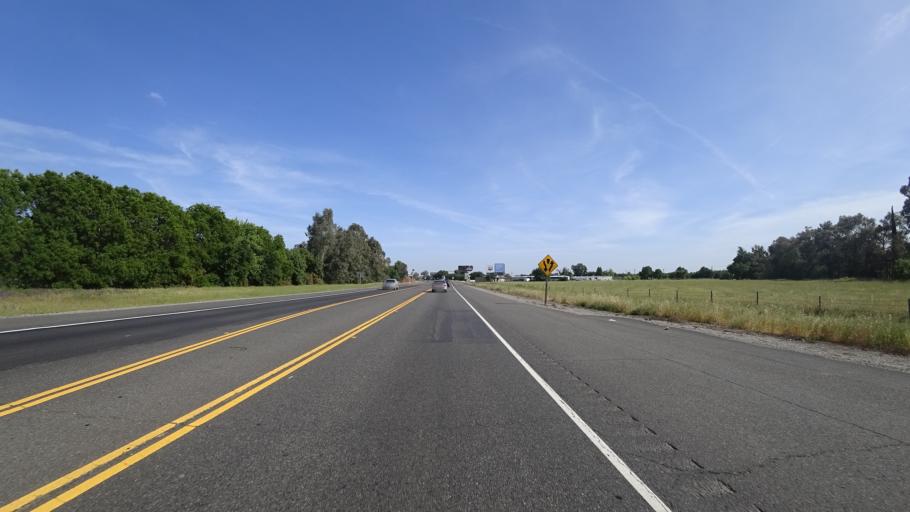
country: US
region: California
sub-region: Butte County
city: Chico
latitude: 39.7892
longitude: -121.8906
